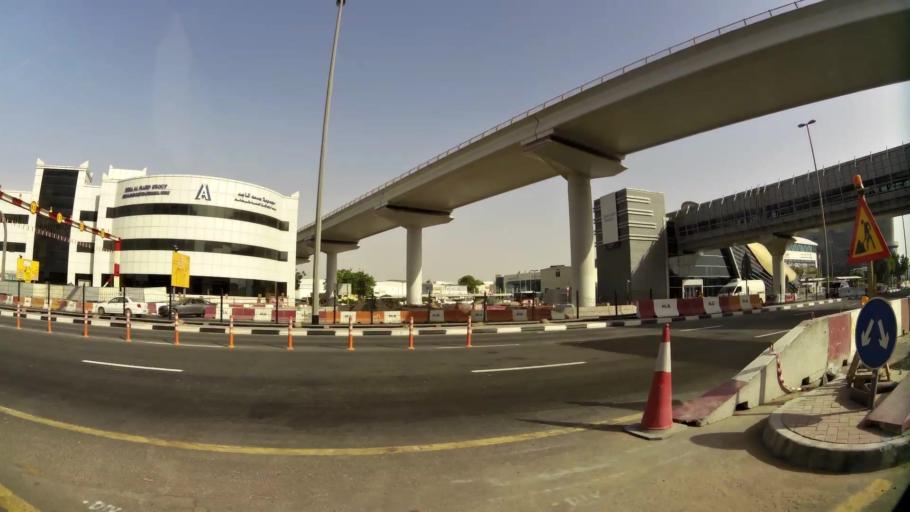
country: AE
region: Ash Shariqah
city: Sharjah
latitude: 25.2404
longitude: 55.3675
